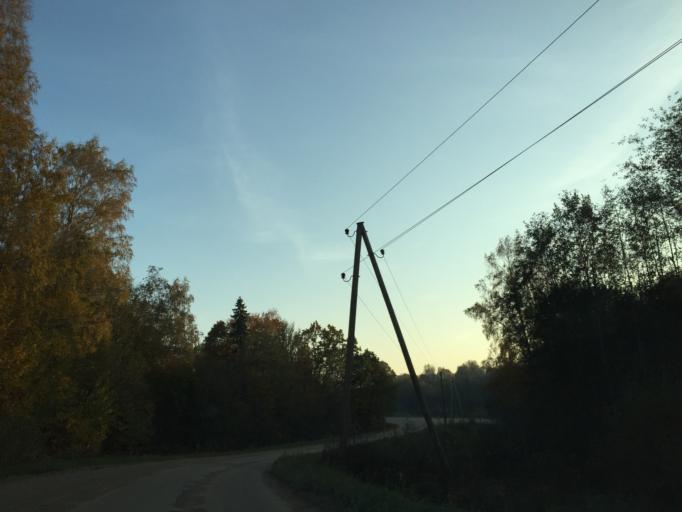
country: LV
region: Vainode
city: Vainode
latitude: 56.5048
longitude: 21.8241
